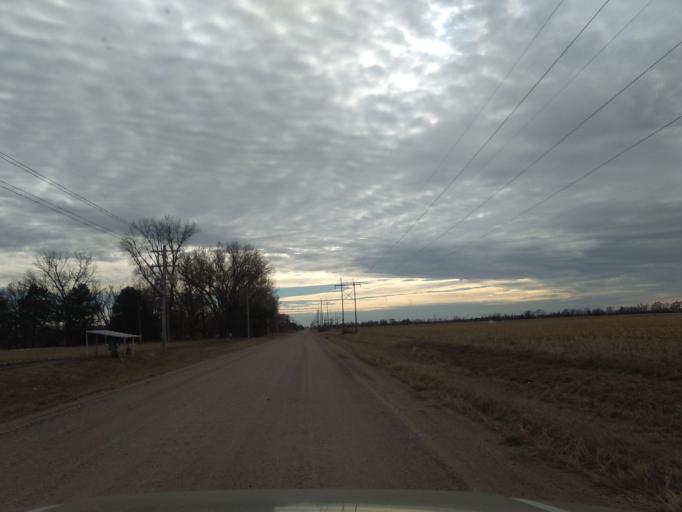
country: US
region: Nebraska
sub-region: Buffalo County
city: Gibbon
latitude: 40.6454
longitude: -98.8759
